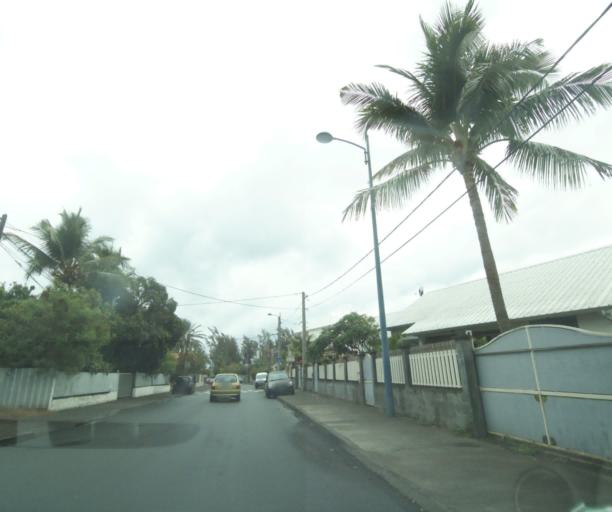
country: RE
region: Reunion
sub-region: Reunion
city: Saint-Paul
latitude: -21.0052
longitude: 55.2770
